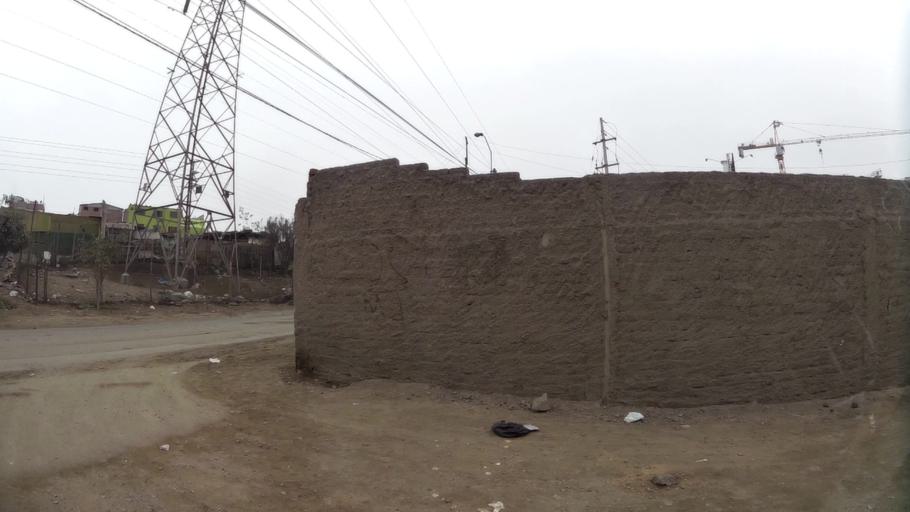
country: PE
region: Lima
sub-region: Lima
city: Surco
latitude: -12.1809
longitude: -76.9439
